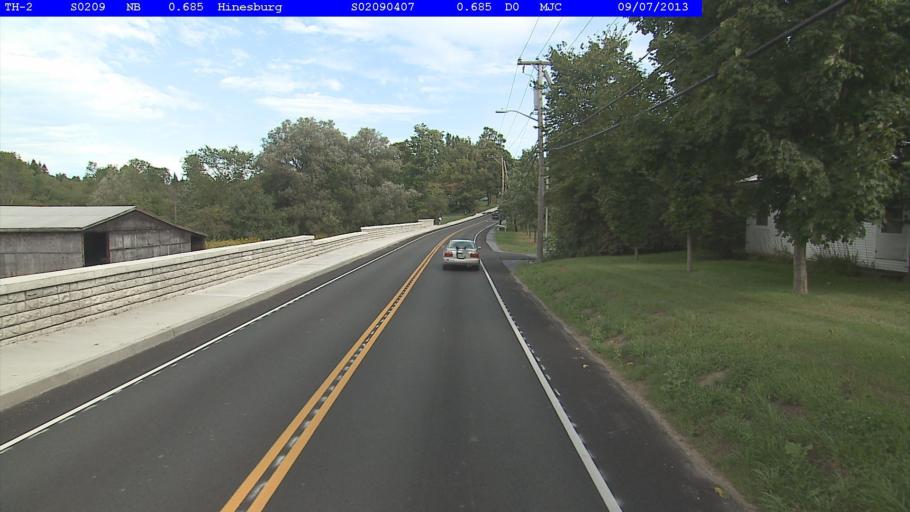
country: US
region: Vermont
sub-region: Chittenden County
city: Hinesburg
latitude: 44.3402
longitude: -73.1059
